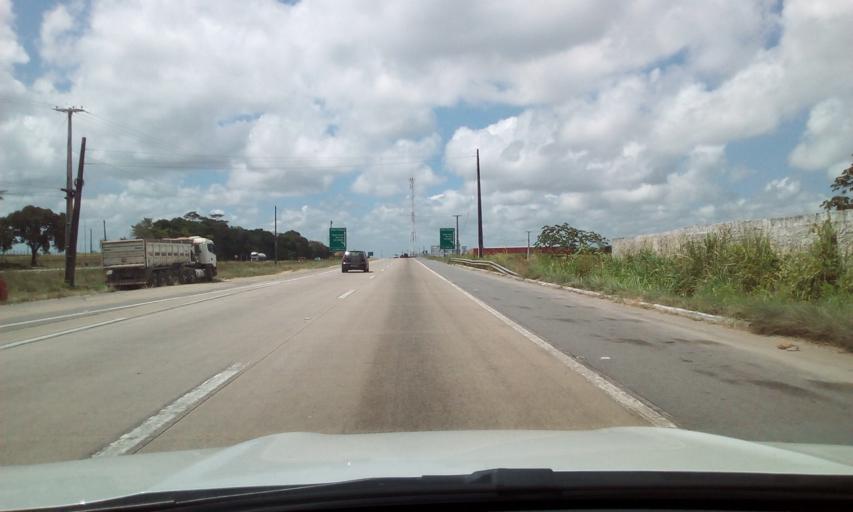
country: BR
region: Pernambuco
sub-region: Itapissuma
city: Itapissuma
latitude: -7.7980
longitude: -34.9268
